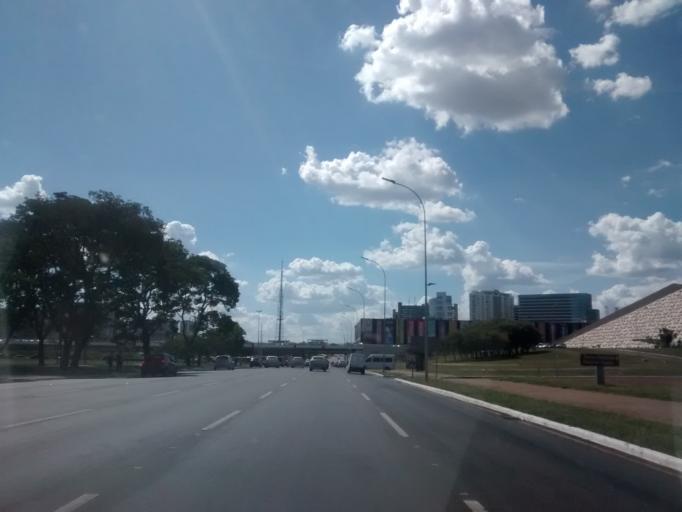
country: BR
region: Federal District
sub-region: Brasilia
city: Brasilia
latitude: -15.7940
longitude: -47.8789
